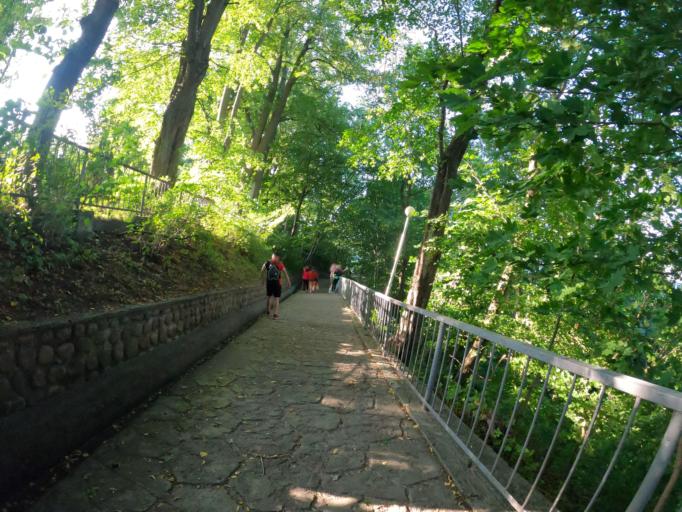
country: RU
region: Kaliningrad
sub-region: Gorod Svetlogorsk
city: Svetlogorsk
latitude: 54.9450
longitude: 20.1520
